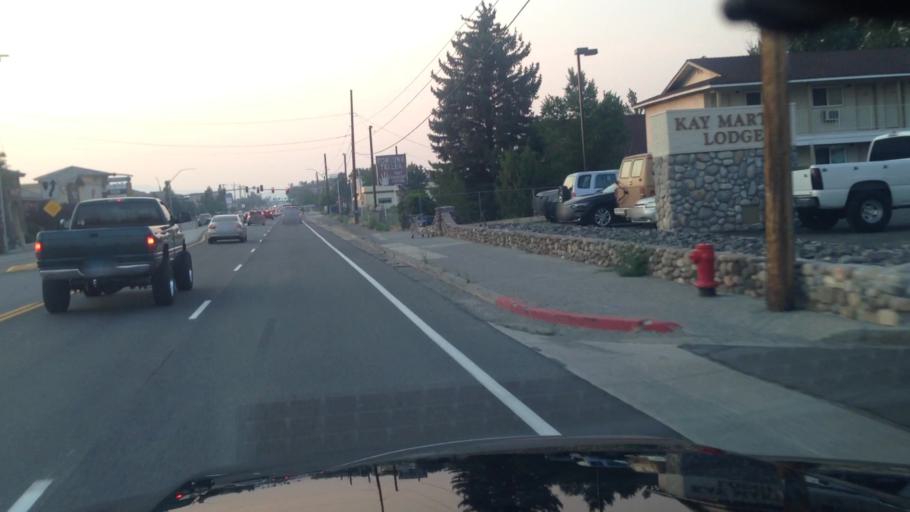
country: US
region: Nevada
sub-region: Washoe County
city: Reno
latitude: 39.4633
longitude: -119.7824
